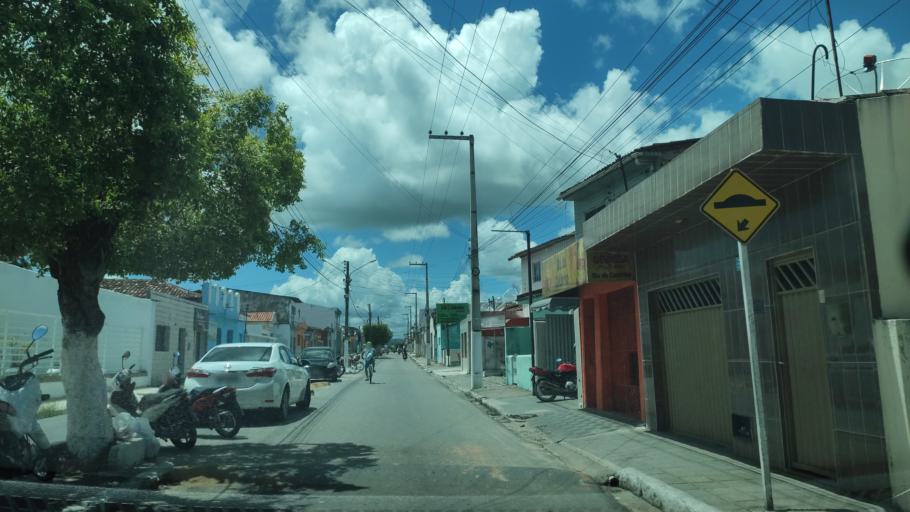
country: BR
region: Alagoas
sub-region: Uniao Dos Palmares
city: Uniao dos Palmares
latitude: -9.1563
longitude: -36.0323
